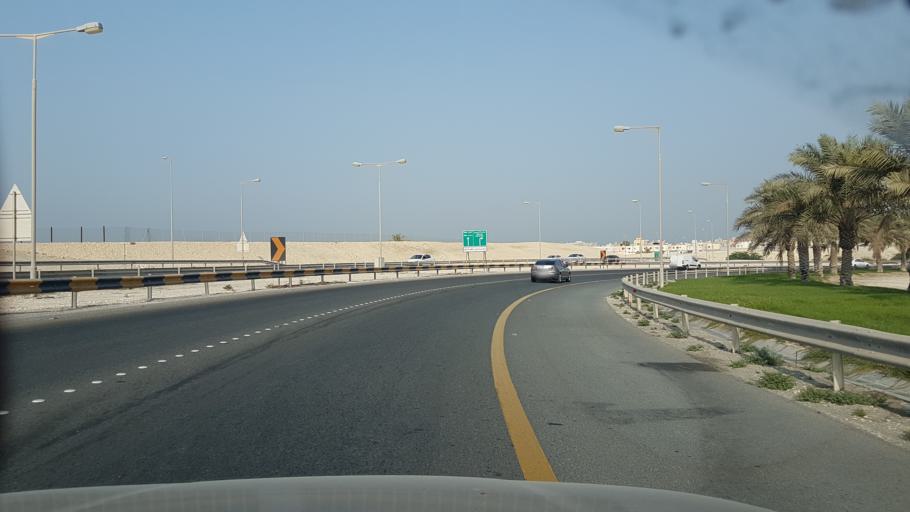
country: BH
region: Central Governorate
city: Dar Kulayb
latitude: 26.0564
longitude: 50.5171
